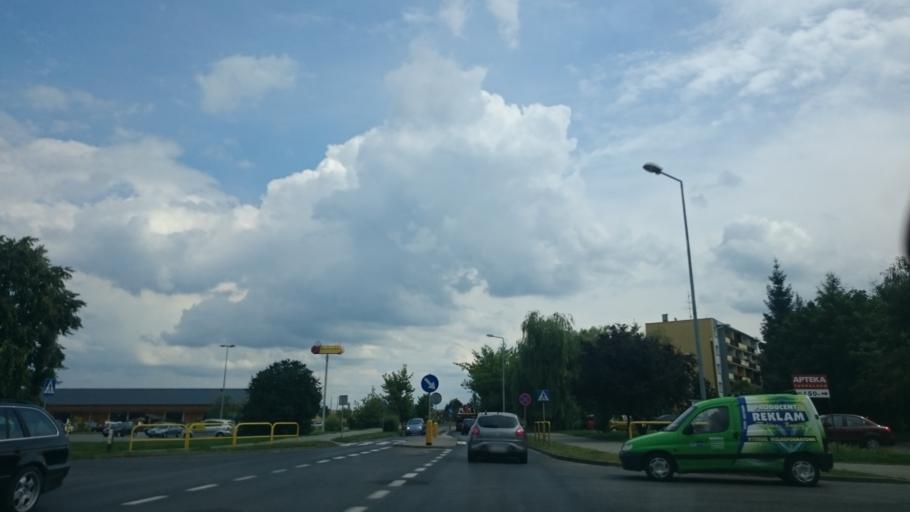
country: PL
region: Kujawsko-Pomorskie
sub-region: Powiat tucholski
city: Tuchola
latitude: 53.5862
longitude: 17.8734
